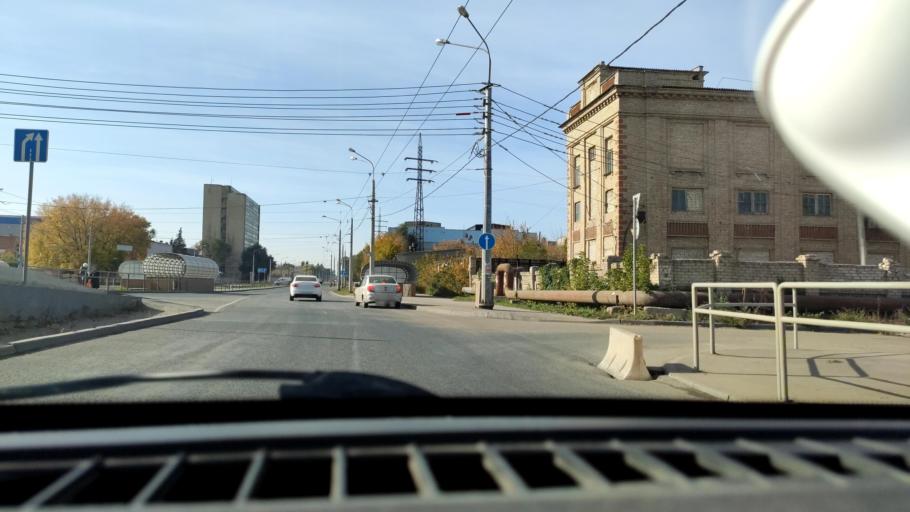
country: RU
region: Samara
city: Smyshlyayevka
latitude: 53.2070
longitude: 50.2751
